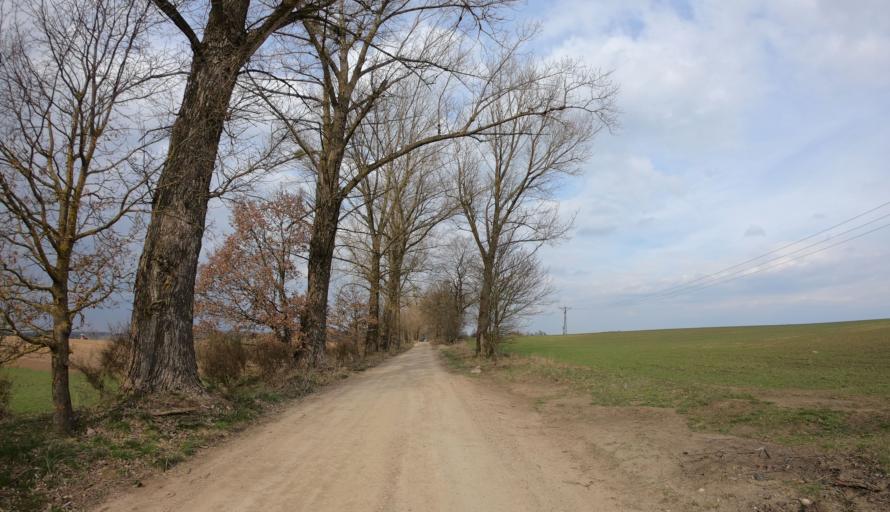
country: PL
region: West Pomeranian Voivodeship
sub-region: Powiat swidwinski
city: Rabino
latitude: 53.8718
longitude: 15.8775
